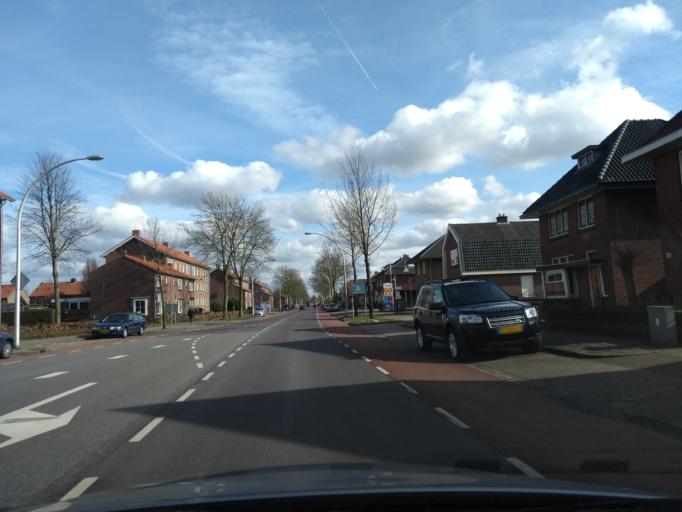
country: NL
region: Overijssel
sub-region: Gemeente Hengelo
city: Hengelo
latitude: 52.2541
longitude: 6.7733
